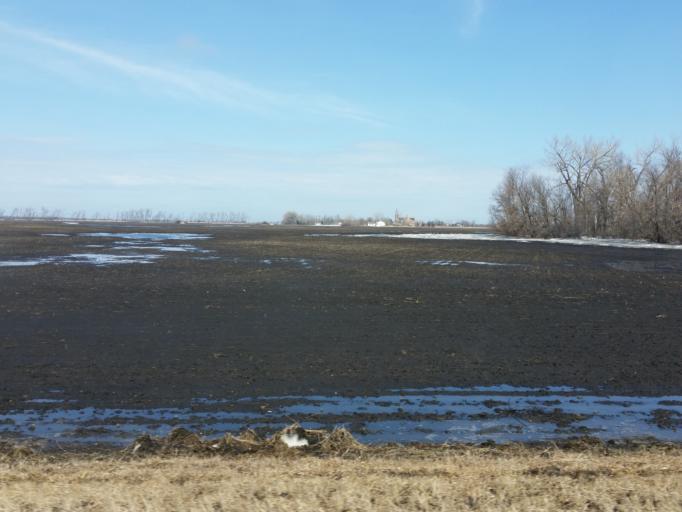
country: US
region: North Dakota
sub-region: Walsh County
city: Grafton
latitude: 48.2809
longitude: -97.2576
